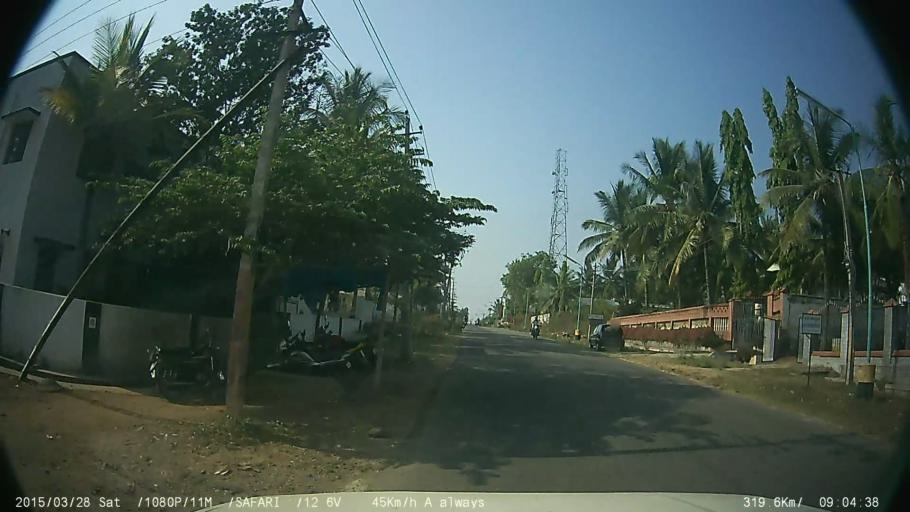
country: IN
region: Karnataka
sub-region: Mysore
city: Mysore
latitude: 12.3517
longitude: 76.5969
